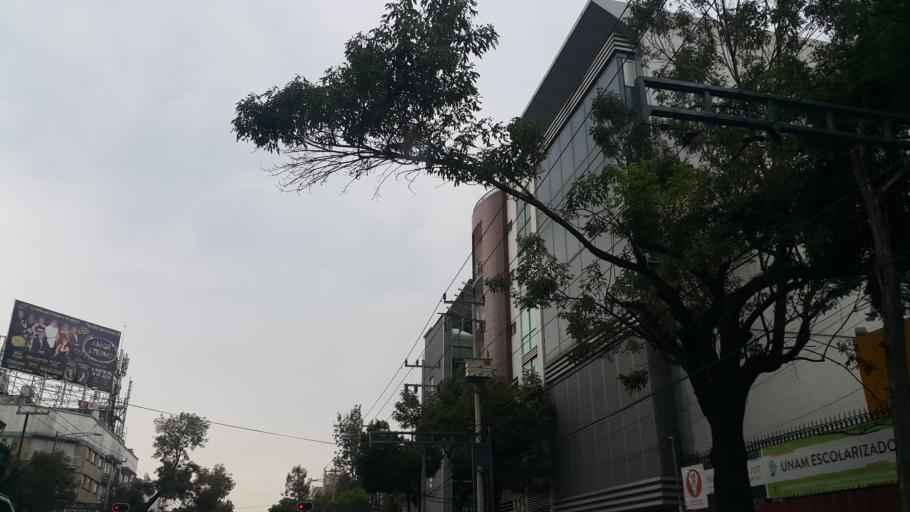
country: MX
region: Mexico City
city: Colonia del Valle
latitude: 19.3678
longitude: -99.1745
